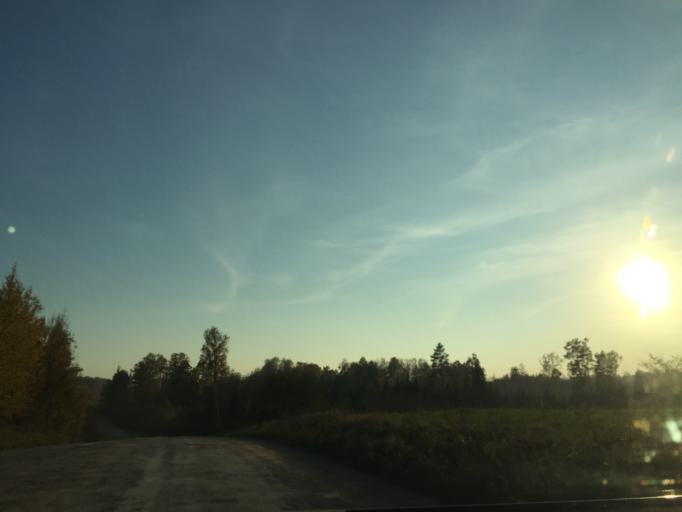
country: LV
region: Vainode
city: Vainode
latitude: 56.5453
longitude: 21.8381
